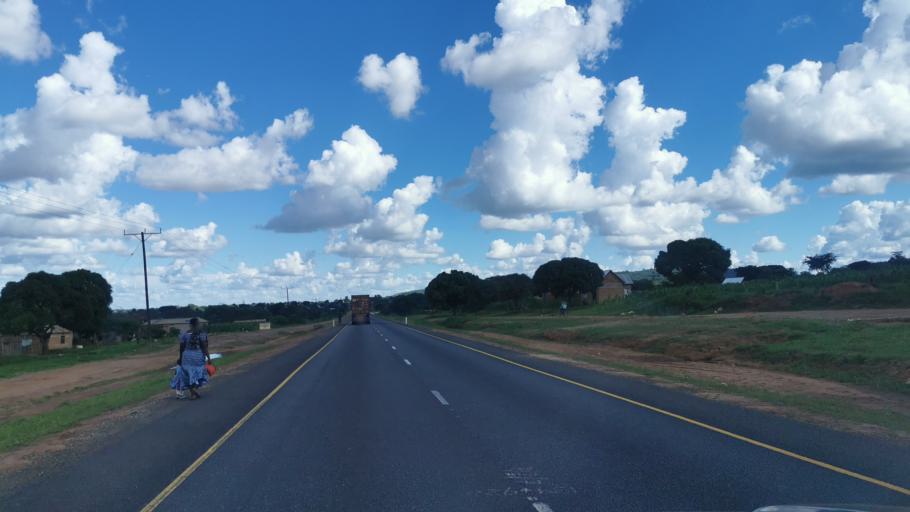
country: TZ
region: Geita
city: Ushirombo
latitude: -3.4366
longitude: 31.8347
